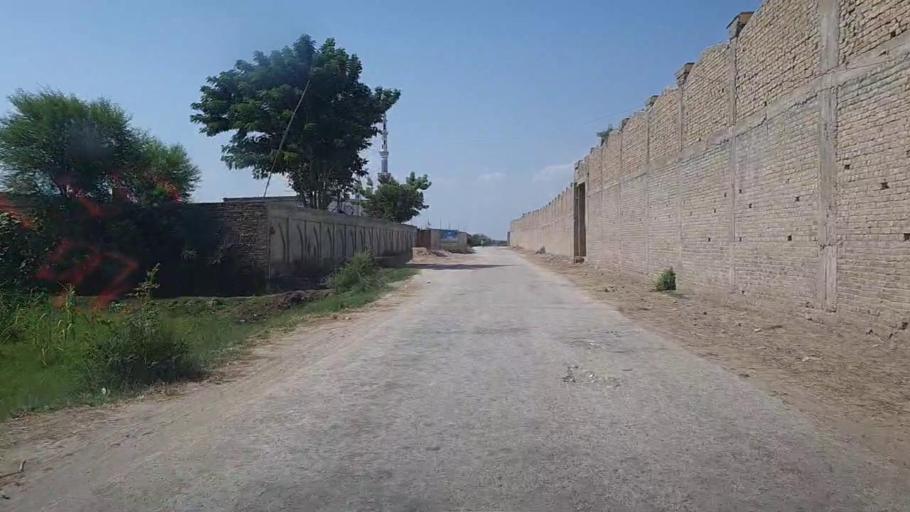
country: PK
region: Sindh
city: Khairpur
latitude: 28.0653
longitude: 69.6445
